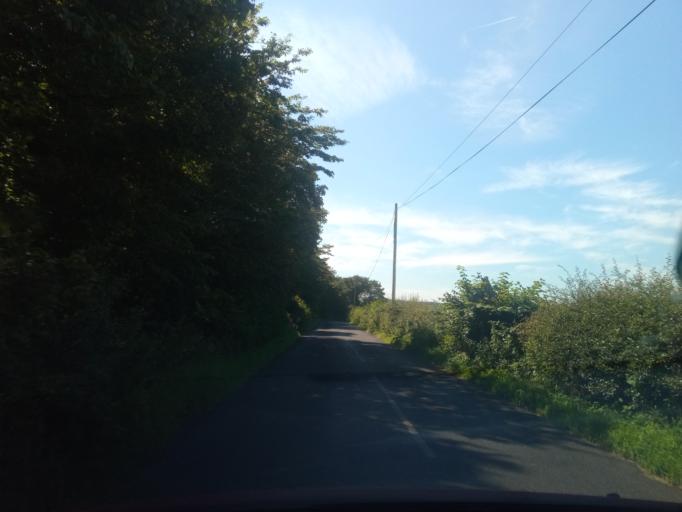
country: GB
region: England
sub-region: Northumberland
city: Warden
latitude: 54.9856
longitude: -2.2238
